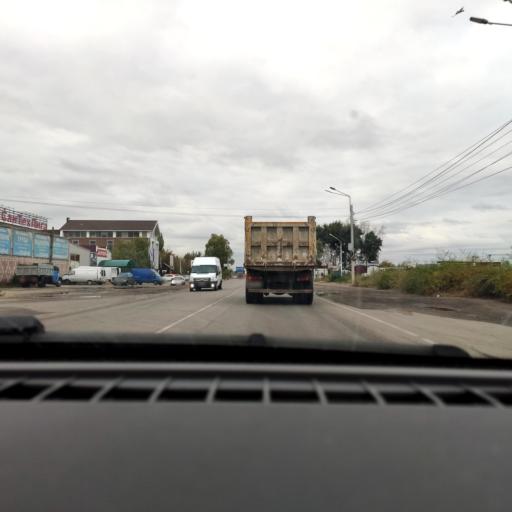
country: RU
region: Voronezj
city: Maslovka
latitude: 51.6428
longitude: 39.2953
